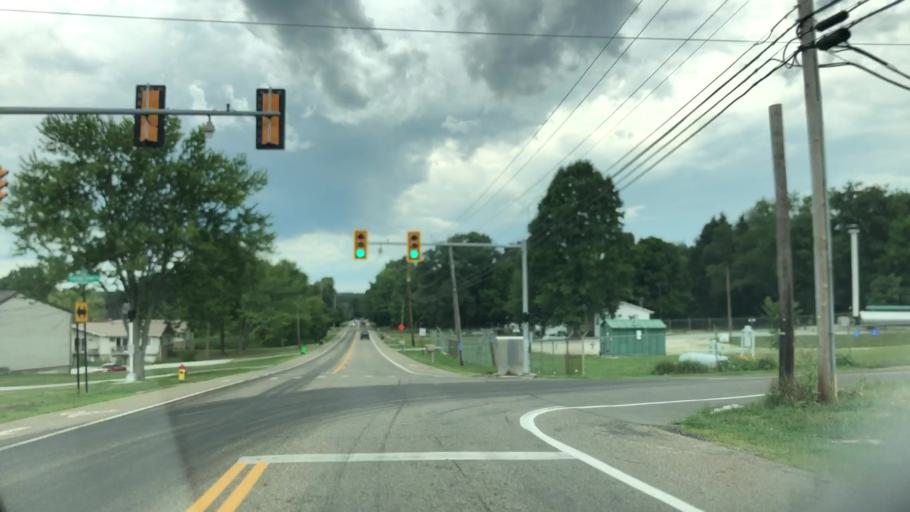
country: US
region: Ohio
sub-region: Summit County
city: New Franklin
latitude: 40.9533
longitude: -81.5136
